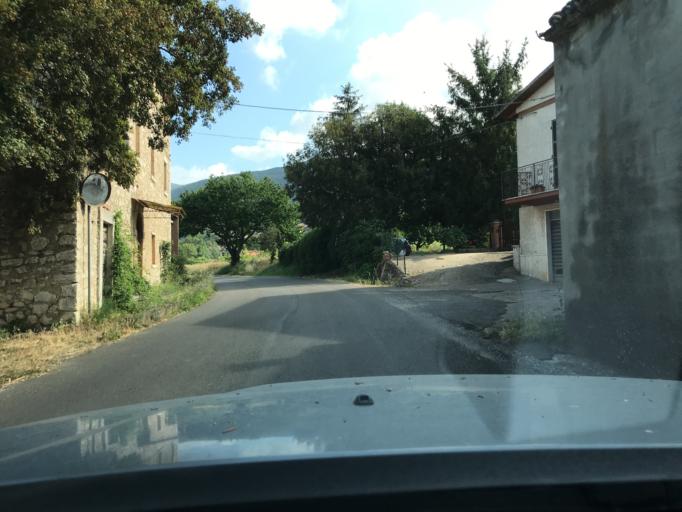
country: IT
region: Umbria
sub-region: Provincia di Terni
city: Guardea
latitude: 42.6254
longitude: 12.3163
